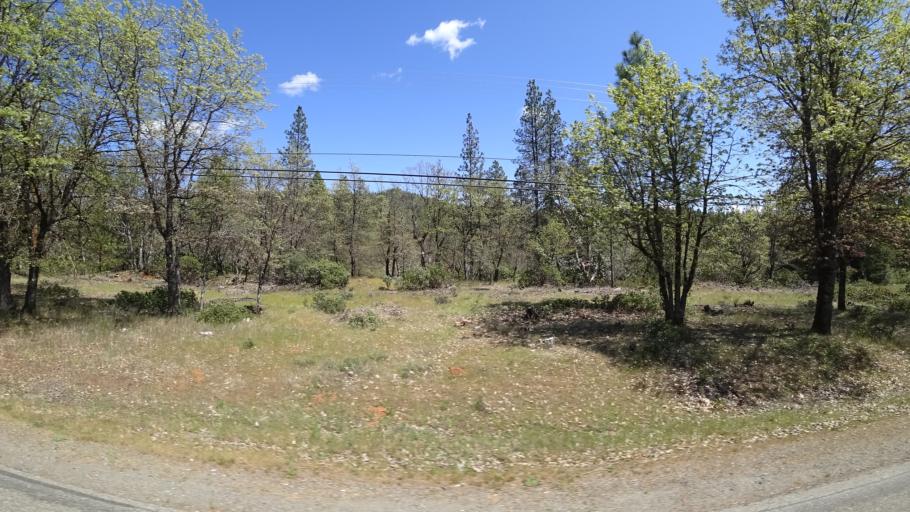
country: US
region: California
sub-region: Trinity County
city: Weaverville
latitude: 40.7473
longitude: -122.9215
